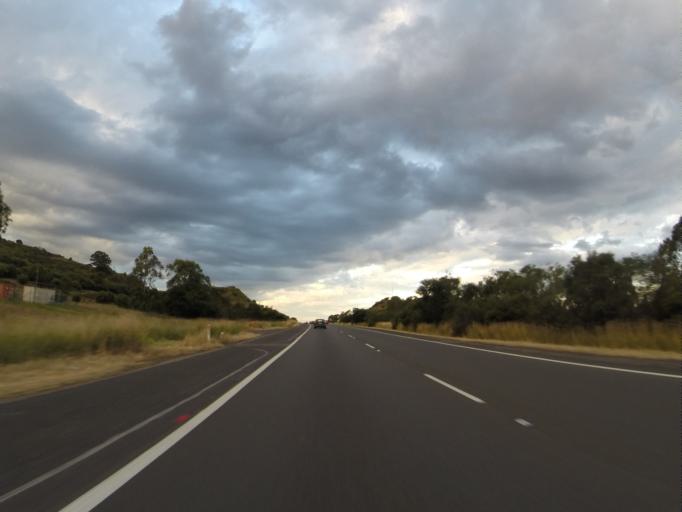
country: AU
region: New South Wales
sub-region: Wollondilly
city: Douglas Park
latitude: -34.1758
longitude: 150.7296
